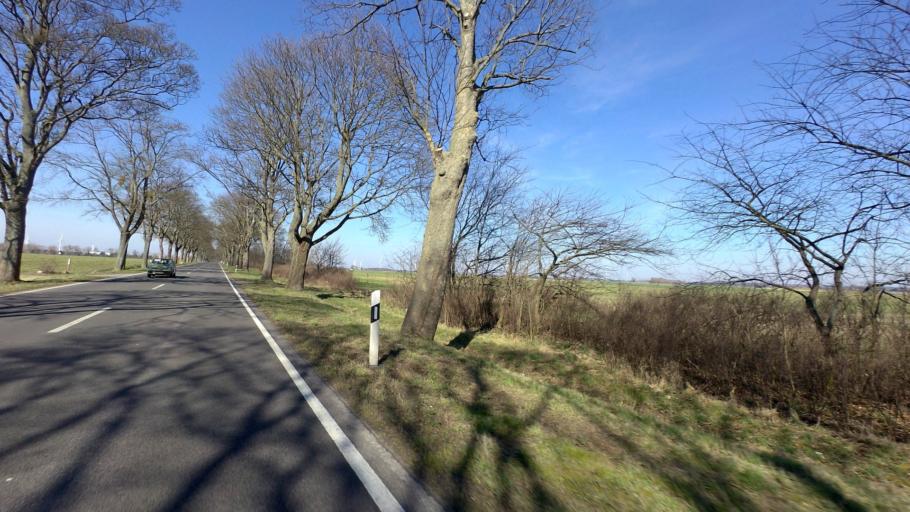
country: DE
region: Brandenburg
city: Werftpfuhl
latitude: 52.7267
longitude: 13.8377
